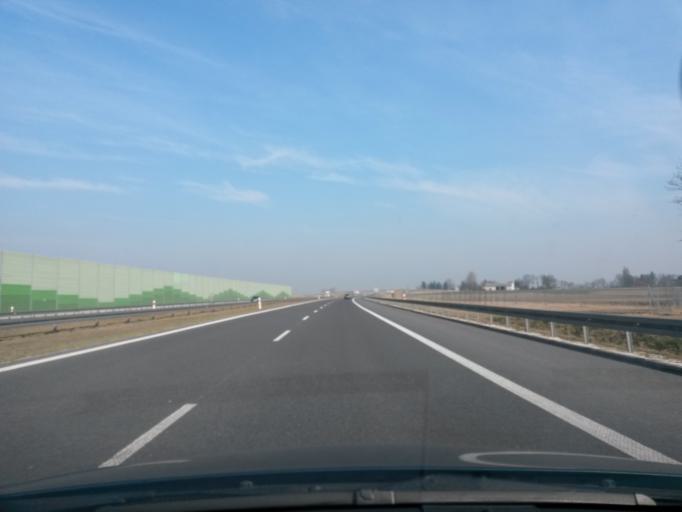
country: PL
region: Lodz Voivodeship
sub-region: Powiat kutnowski
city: Krzyzanow
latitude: 52.1484
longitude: 19.4817
